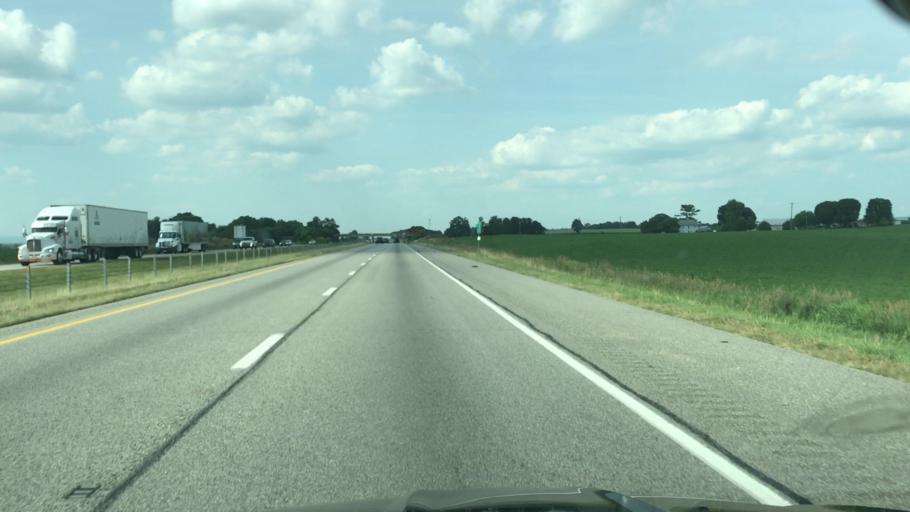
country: US
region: Pennsylvania
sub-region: Franklin County
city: Guilford Siding
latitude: 39.8720
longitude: -77.6797
